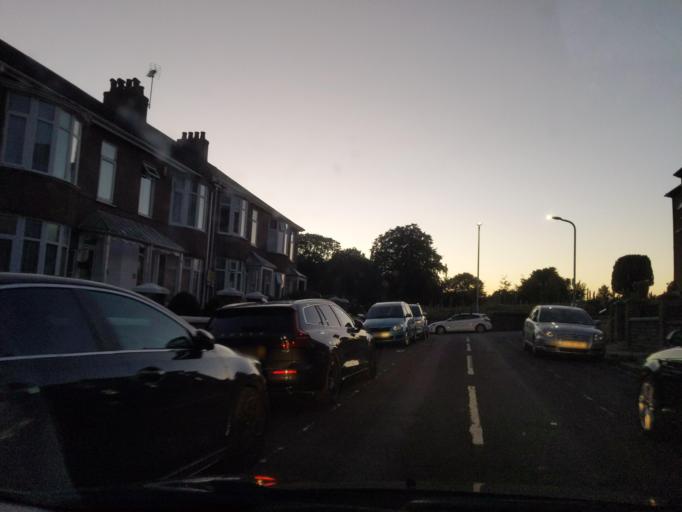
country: GB
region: England
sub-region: Plymouth
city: Plymouth
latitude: 50.3814
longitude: -4.1435
